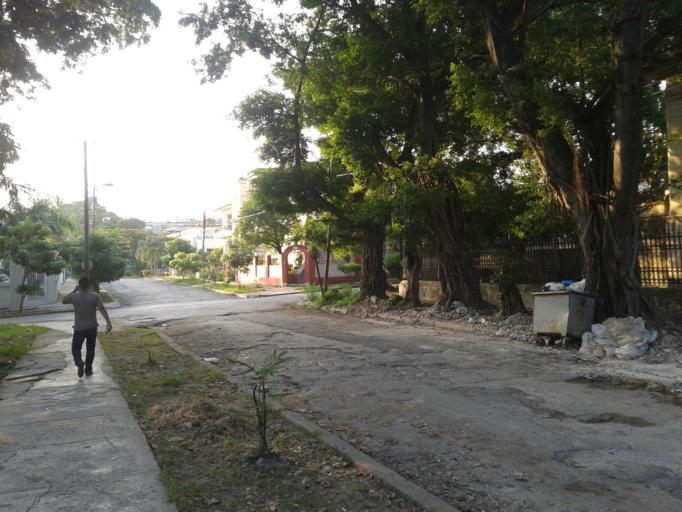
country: CU
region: La Habana
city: Cerro
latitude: 23.0933
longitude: -82.3746
